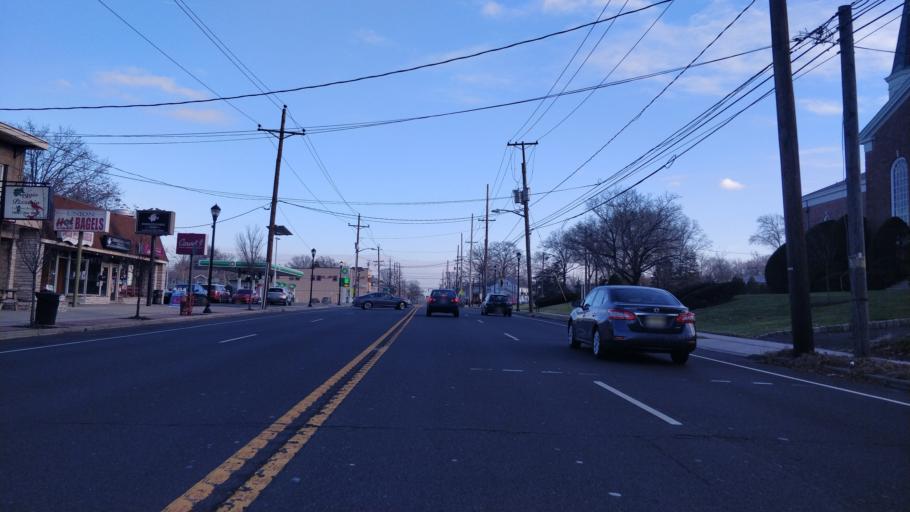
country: US
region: New Jersey
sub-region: Union County
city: Union
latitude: 40.6914
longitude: -74.2530
